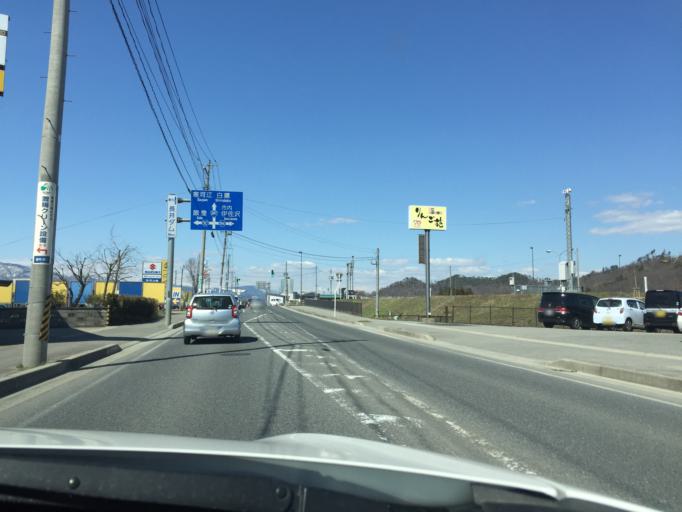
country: JP
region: Yamagata
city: Nagai
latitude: 38.0947
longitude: 140.0415
